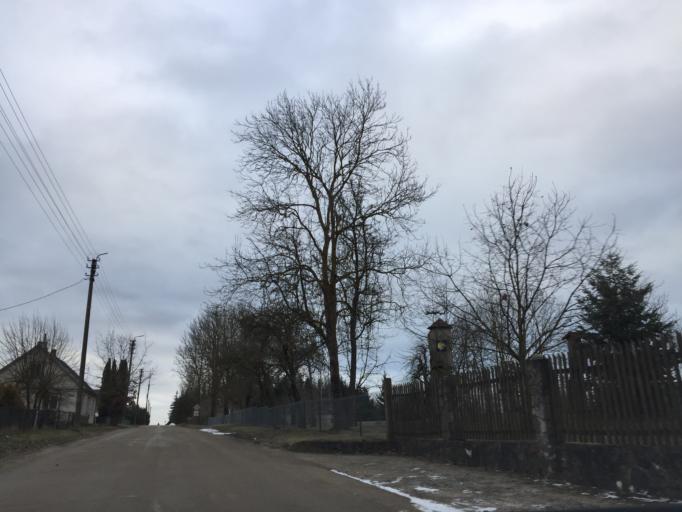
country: LT
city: Zagare
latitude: 56.3567
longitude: 23.2551
